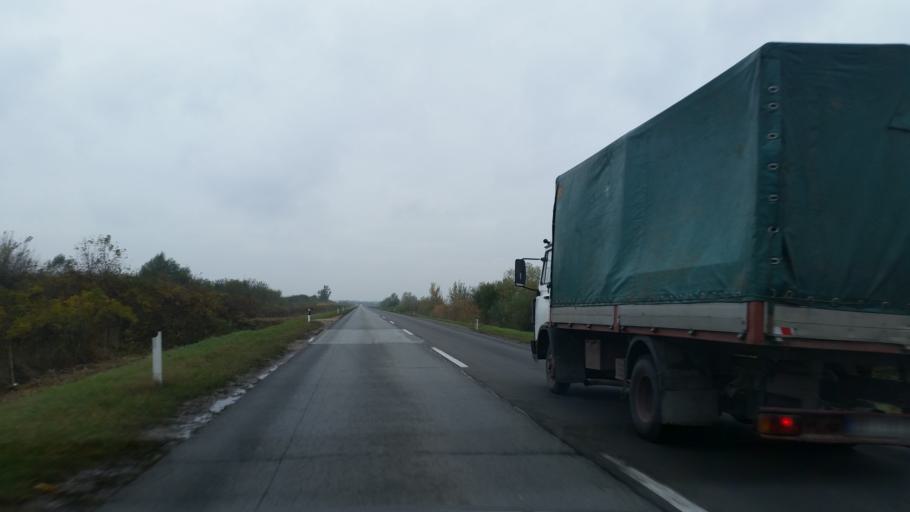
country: RS
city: Sefkerin
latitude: 44.9587
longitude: 20.4250
